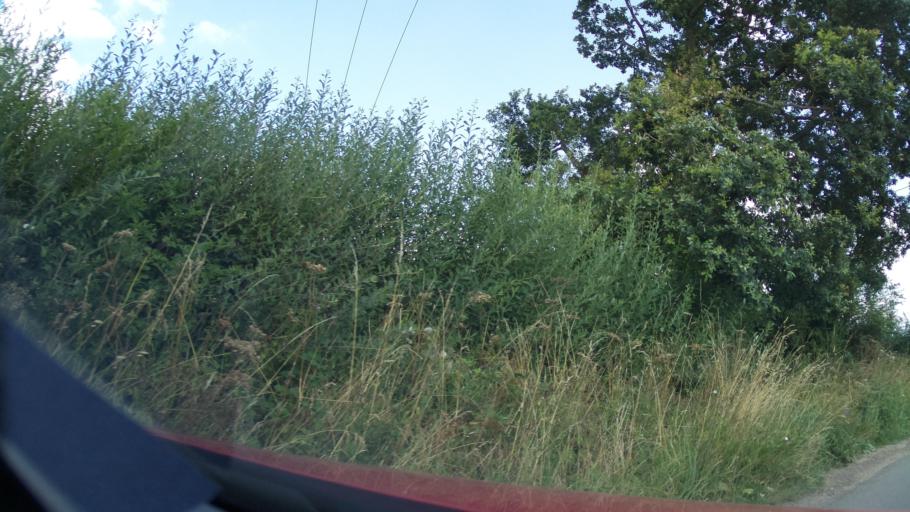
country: GB
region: England
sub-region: Wiltshire
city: Malmesbury
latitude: 51.5769
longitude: -2.1181
